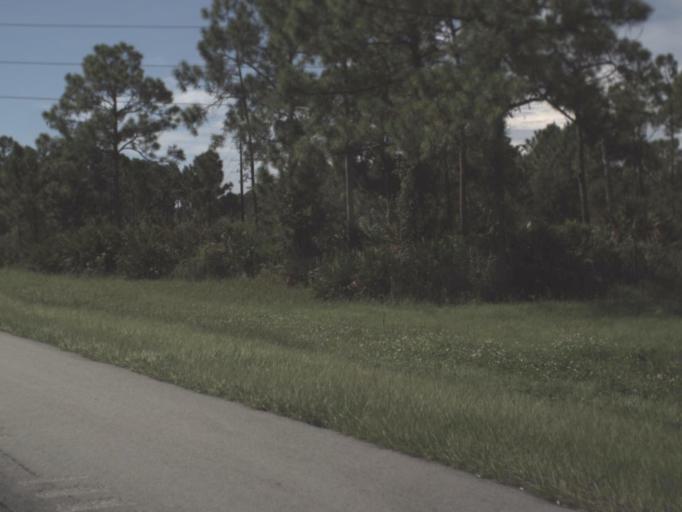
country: US
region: Florida
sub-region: Charlotte County
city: Charlotte Park
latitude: 26.8662
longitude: -81.9733
